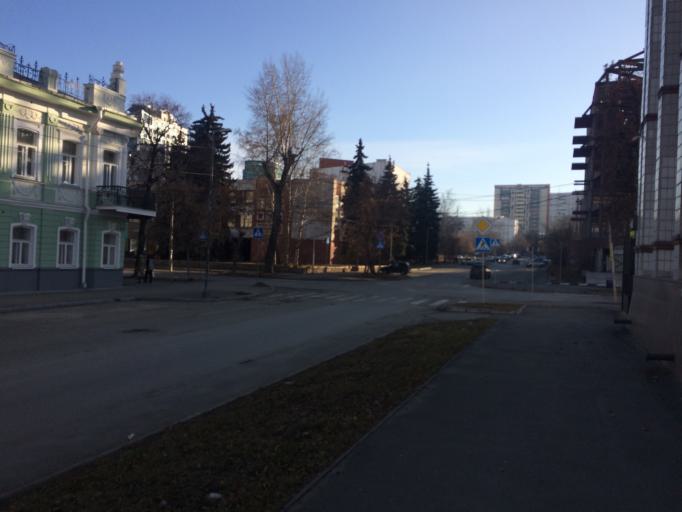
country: RU
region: Chelyabinsk
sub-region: Gorod Chelyabinsk
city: Chelyabinsk
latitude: 55.1631
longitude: 61.3958
